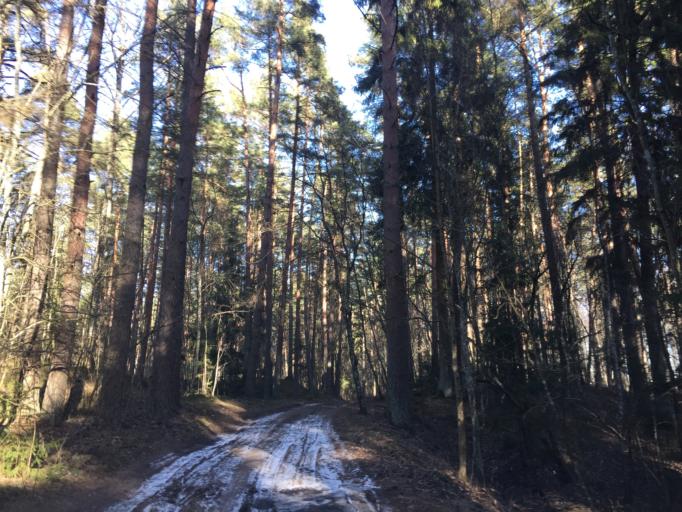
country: LV
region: Babite
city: Pinki
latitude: 56.9686
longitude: 23.8862
